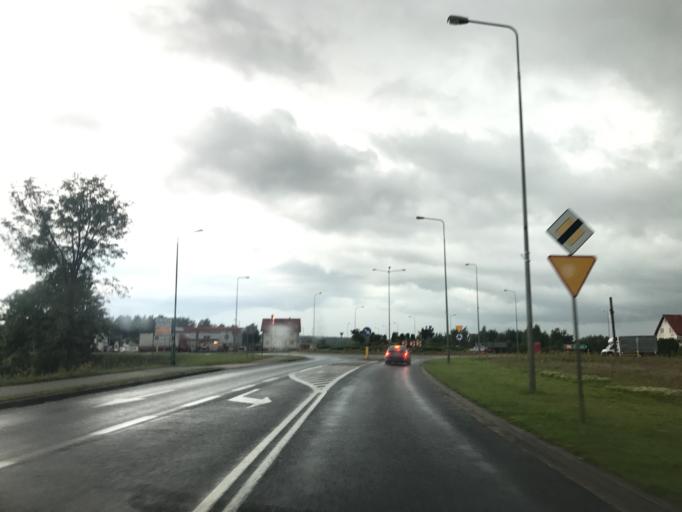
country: PL
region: West Pomeranian Voivodeship
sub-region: Powiat szczecinecki
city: Bialy Bor
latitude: 53.9005
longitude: 16.8410
